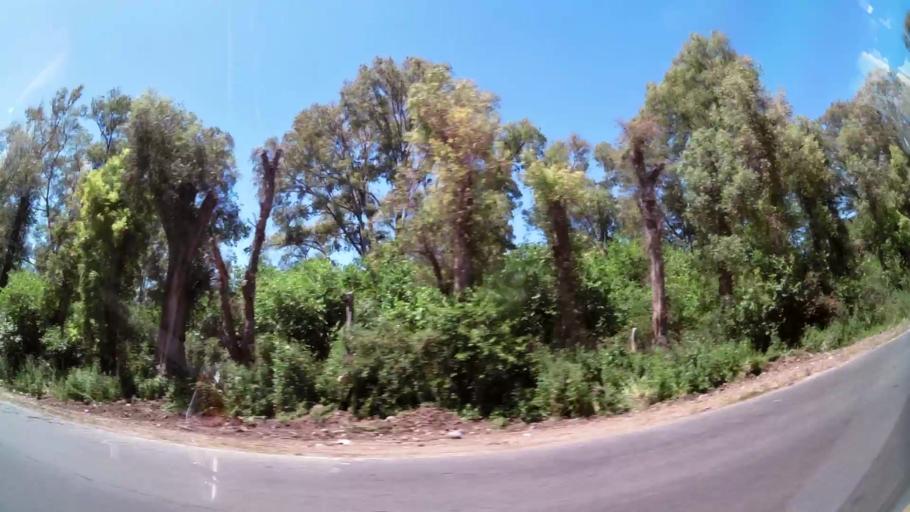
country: AR
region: Buenos Aires
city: Hurlingham
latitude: -34.5074
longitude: -58.6552
